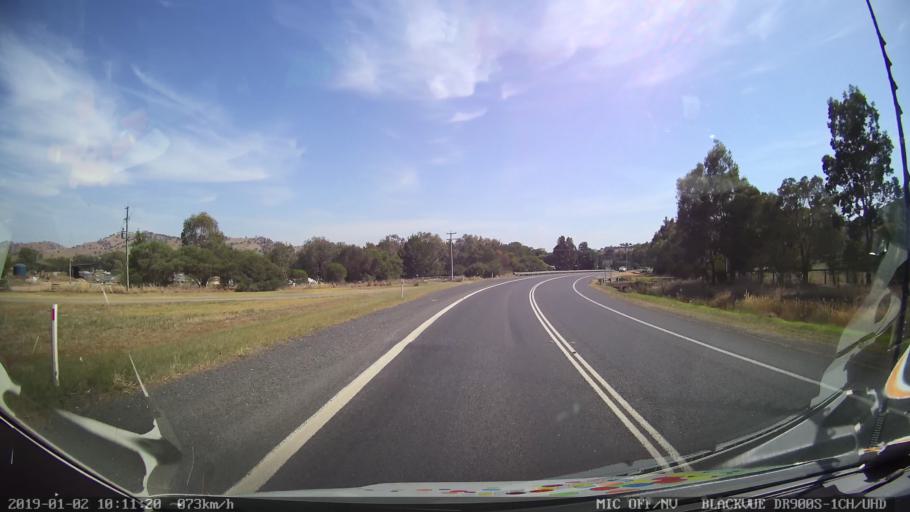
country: AU
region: New South Wales
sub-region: Gundagai
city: Gundagai
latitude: -35.0937
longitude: 148.0918
